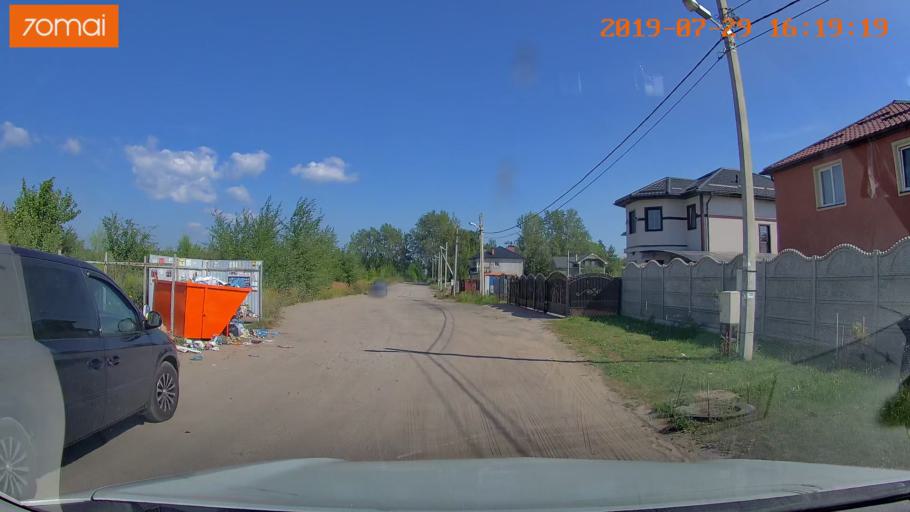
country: RU
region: Kaliningrad
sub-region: Gorod Kaliningrad
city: Baltiysk
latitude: 54.6795
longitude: 19.9231
